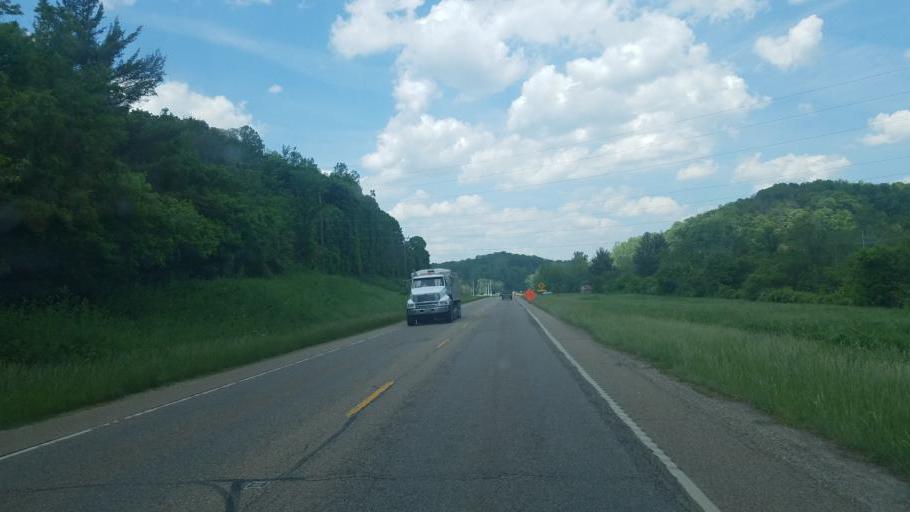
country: US
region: Ohio
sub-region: Meigs County
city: Pomeroy
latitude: 39.0304
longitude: -82.0650
